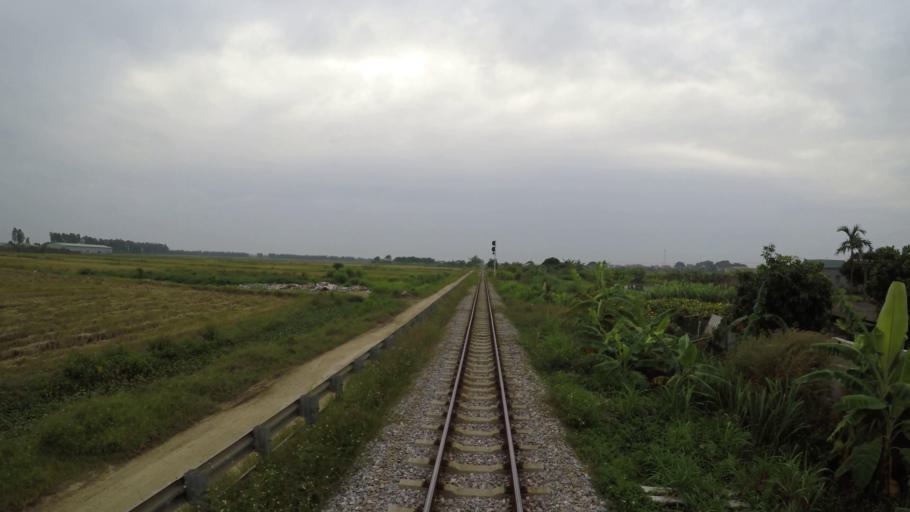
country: VN
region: Bac Ninh
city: Thua
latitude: 20.9663
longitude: 106.1726
